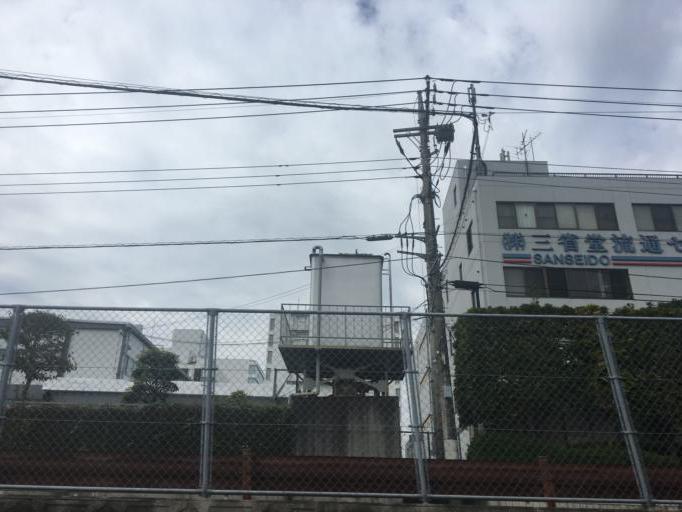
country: JP
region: Tokyo
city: Hachioji
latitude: 35.6665
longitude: 139.3616
